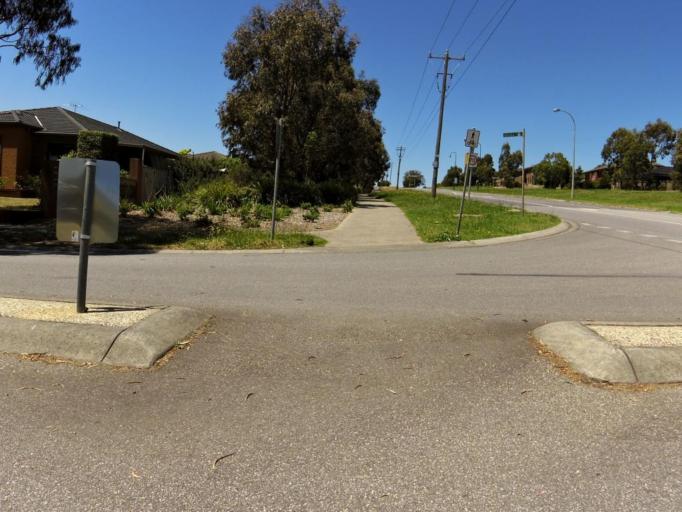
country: AU
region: Victoria
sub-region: Casey
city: Berwick
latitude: -38.0615
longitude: 145.3505
